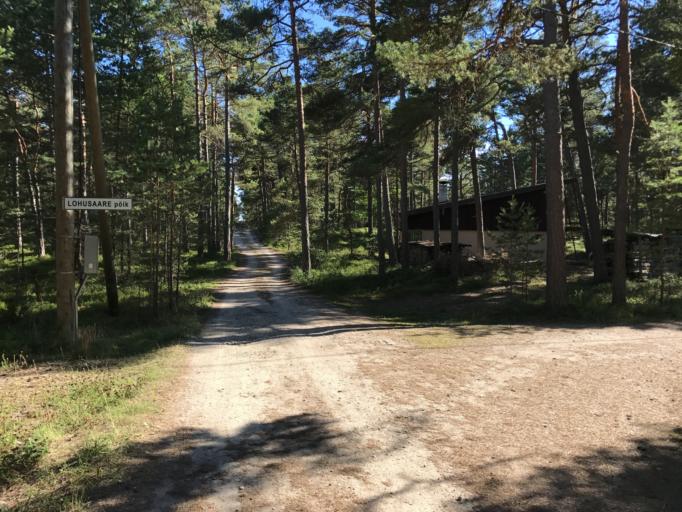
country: EE
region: Harju
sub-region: Paldiski linn
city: Paldiski
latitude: 59.3850
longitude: 24.2243
